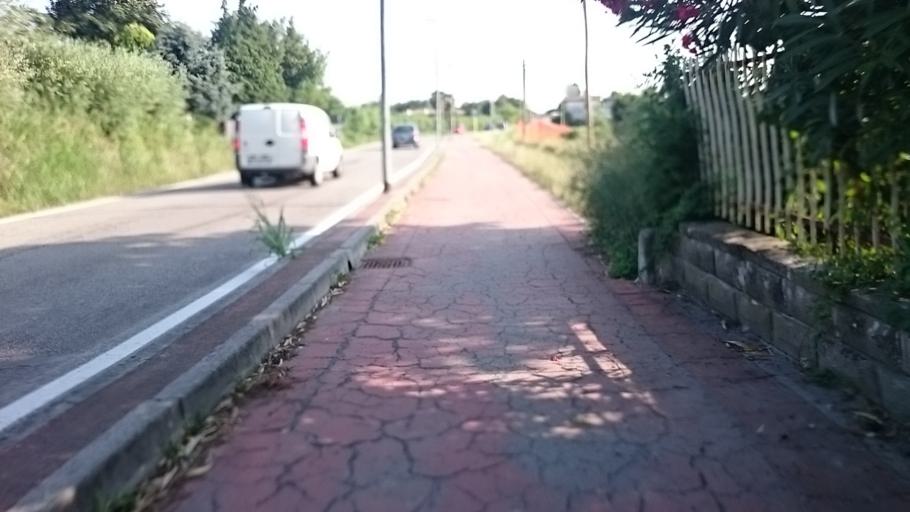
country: IT
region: Veneto
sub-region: Provincia di Venezia
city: Galta
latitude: 45.3896
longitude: 12.0178
